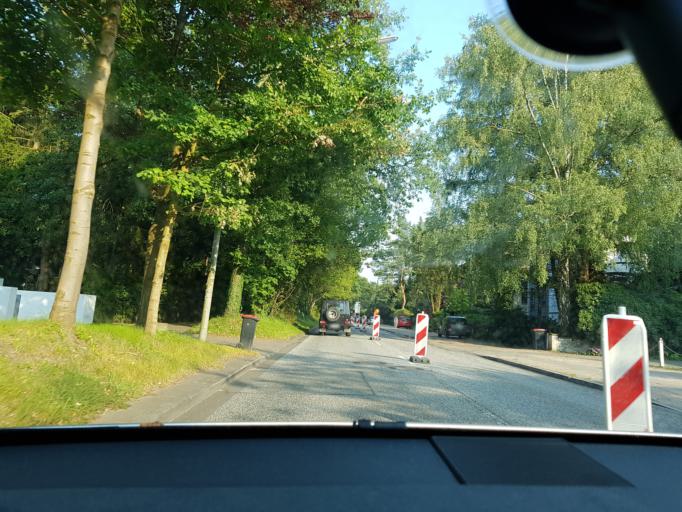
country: DE
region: Hamburg
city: Wellingsbuettel
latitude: 53.6400
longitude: 10.0864
